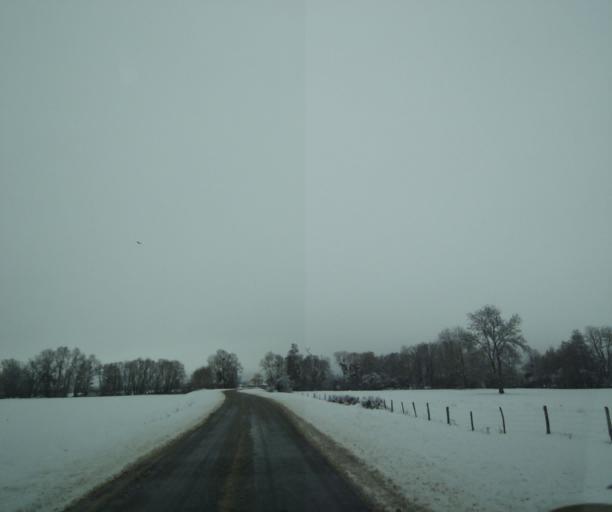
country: FR
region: Champagne-Ardenne
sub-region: Departement de la Haute-Marne
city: Saint-Dizier
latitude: 48.5754
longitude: 4.8908
